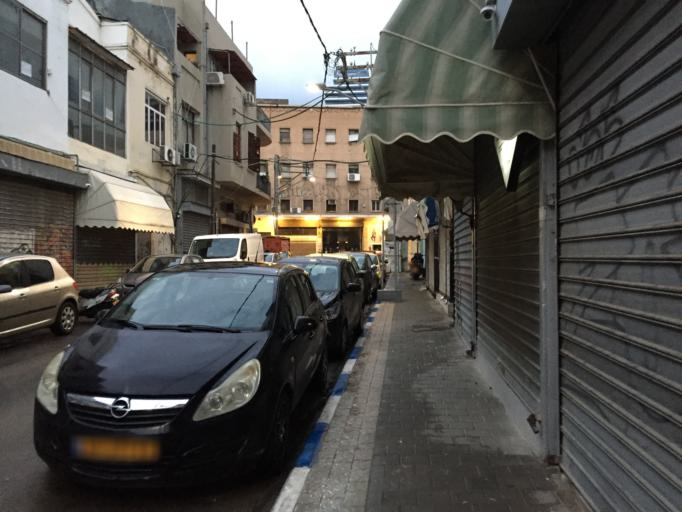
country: IL
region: Tel Aviv
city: Yafo
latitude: 32.0598
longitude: 34.7697
